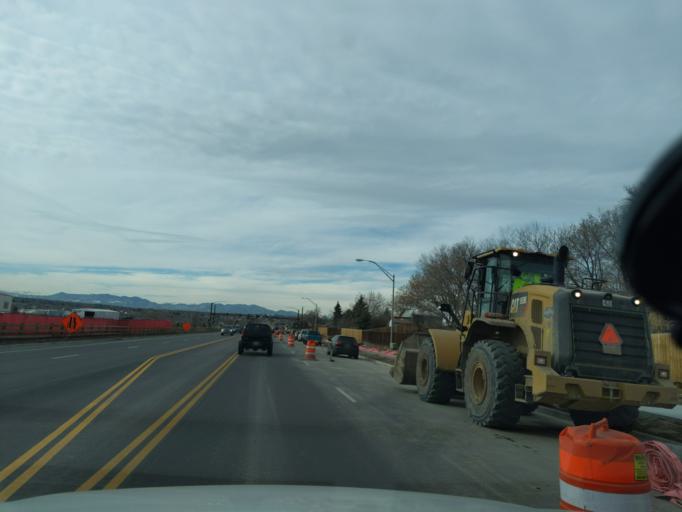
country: US
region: Colorado
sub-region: Adams County
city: Thornton
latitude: 39.8992
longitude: -104.9422
